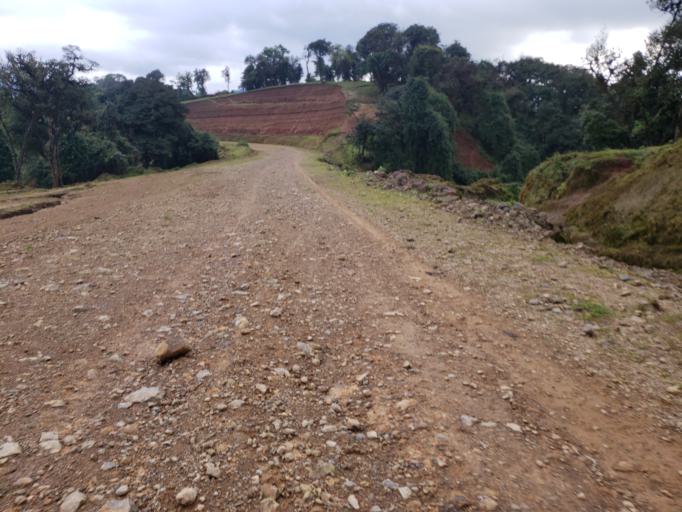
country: ET
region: Oromiya
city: Dodola
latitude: 6.6754
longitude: 39.3636
